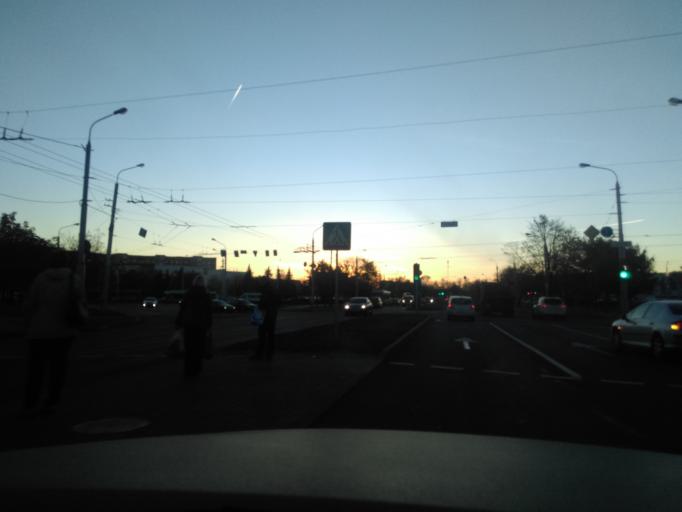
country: BY
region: Minsk
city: Minsk
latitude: 53.8763
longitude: 27.5983
